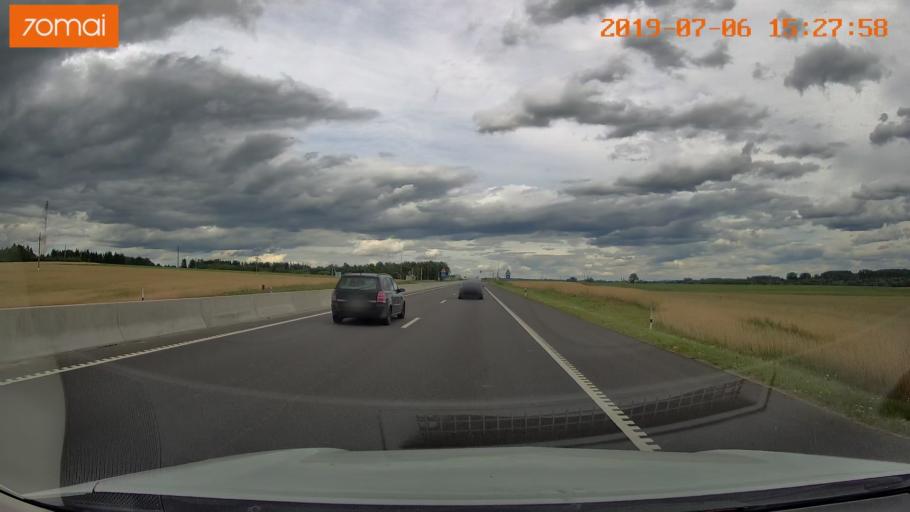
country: BY
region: Minsk
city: Valozhyn
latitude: 54.0386
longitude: 26.6488
